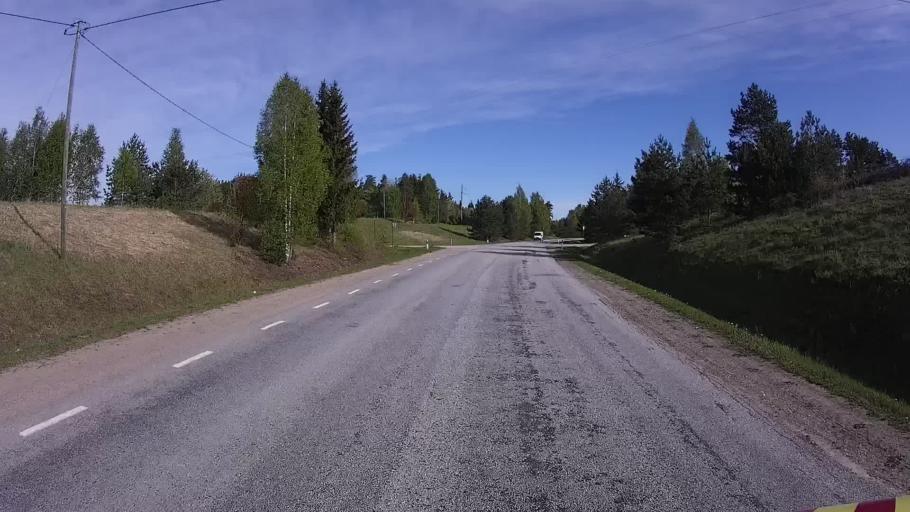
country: EE
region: Tartu
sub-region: Elva linn
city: Elva
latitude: 58.0854
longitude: 26.4915
